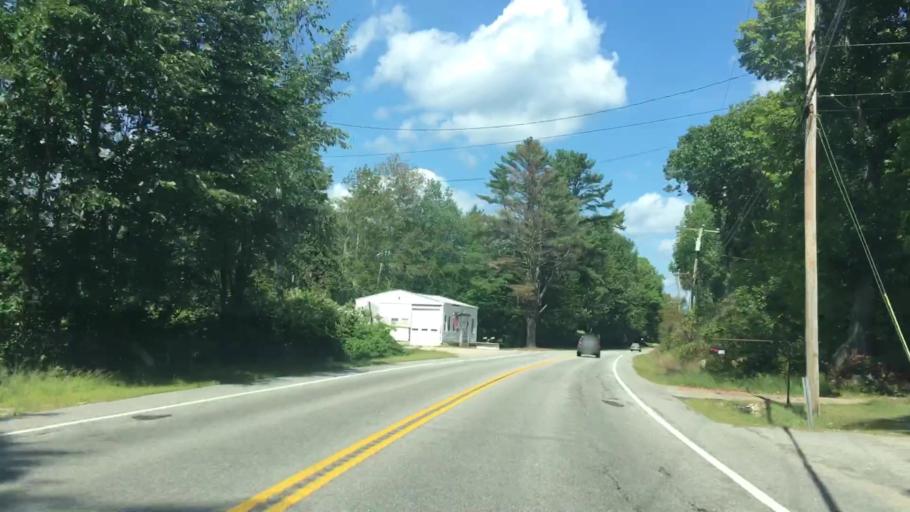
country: US
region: Maine
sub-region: Cumberland County
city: New Gloucester
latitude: 43.9100
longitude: -70.3244
